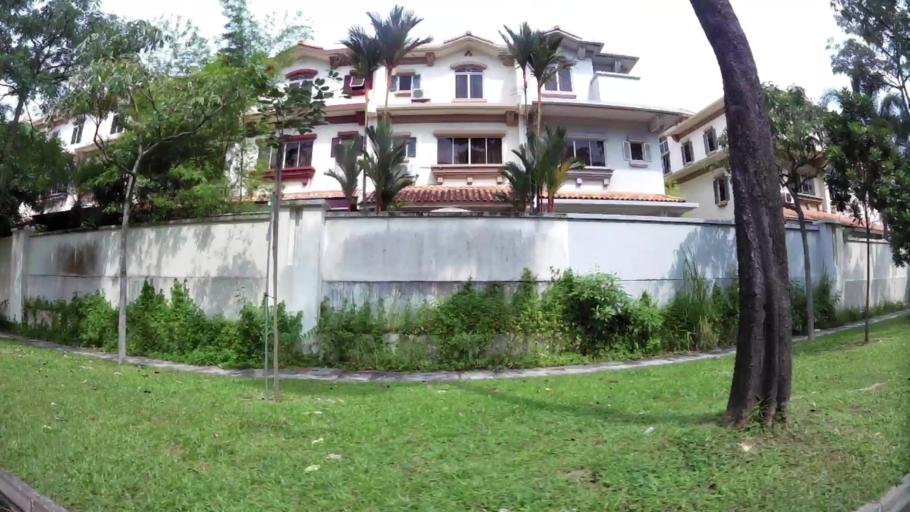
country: SG
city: Singapore
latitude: 1.3623
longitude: 103.9728
